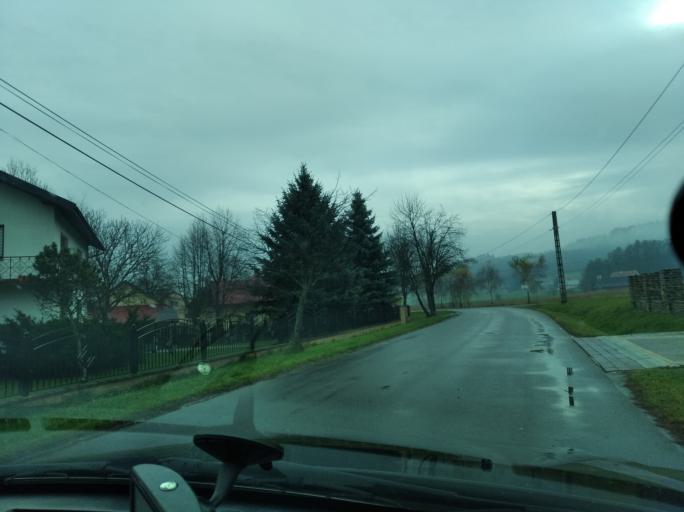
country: PL
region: Subcarpathian Voivodeship
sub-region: Powiat strzyzowski
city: Babica
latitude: 49.9268
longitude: 21.8564
